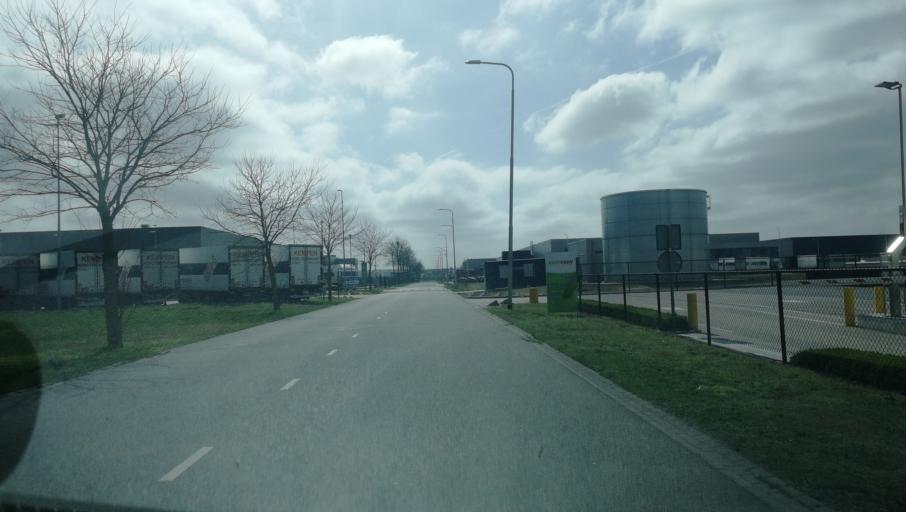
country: NL
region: Limburg
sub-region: Gemeente Venlo
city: Venlo
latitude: 51.4140
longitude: 6.1323
